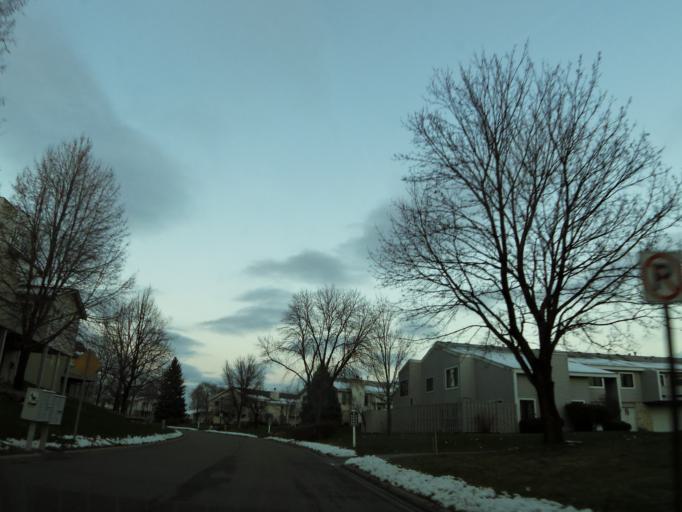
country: US
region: Minnesota
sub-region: Hennepin County
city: Minnetonka Mills
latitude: 44.9046
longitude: -93.4257
